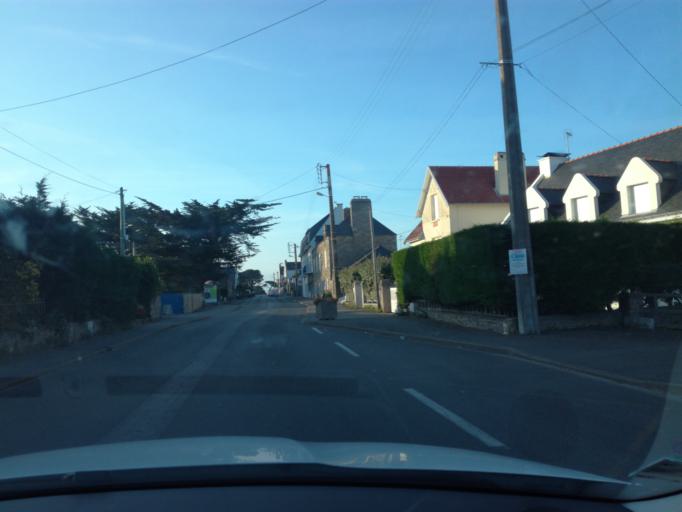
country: FR
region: Brittany
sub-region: Departement du Morbihan
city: Saint-Pierre-Quiberon
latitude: 47.5350
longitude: -3.1349
